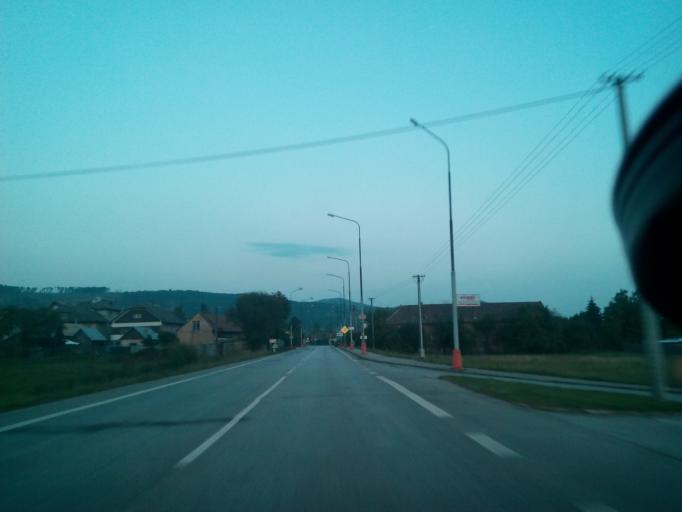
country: SK
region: Kosicky
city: Roznava
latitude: 48.7027
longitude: 20.5010
